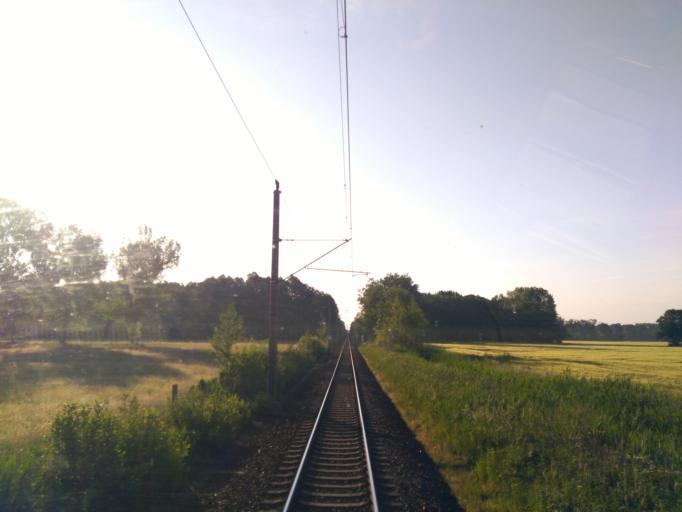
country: DE
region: Brandenburg
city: Kolkwitz
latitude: 51.7561
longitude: 14.2580
